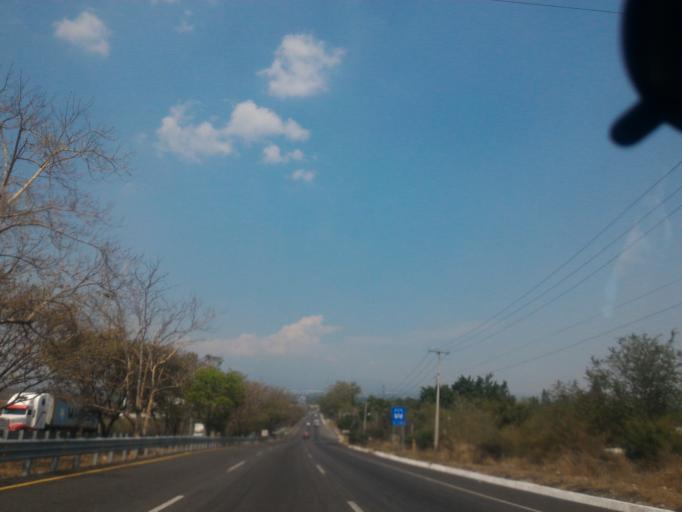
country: MX
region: Colima
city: Coquimatlan
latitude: 19.1860
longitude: -103.7521
